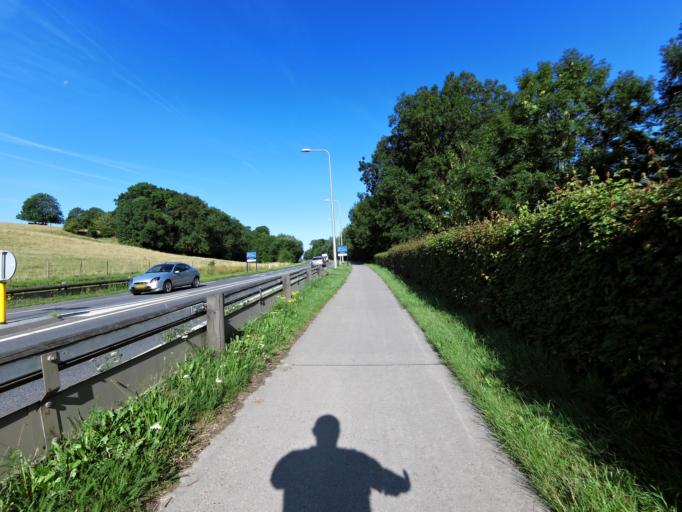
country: NL
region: Limburg
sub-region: Gemeente Simpelveld
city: Simpelveld
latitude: 50.8080
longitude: 5.9536
